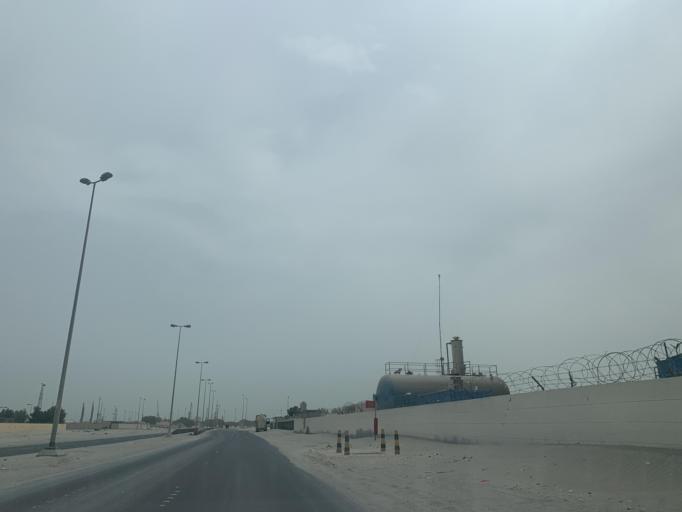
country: BH
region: Muharraq
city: Al Hadd
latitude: 26.2054
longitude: 50.6597
